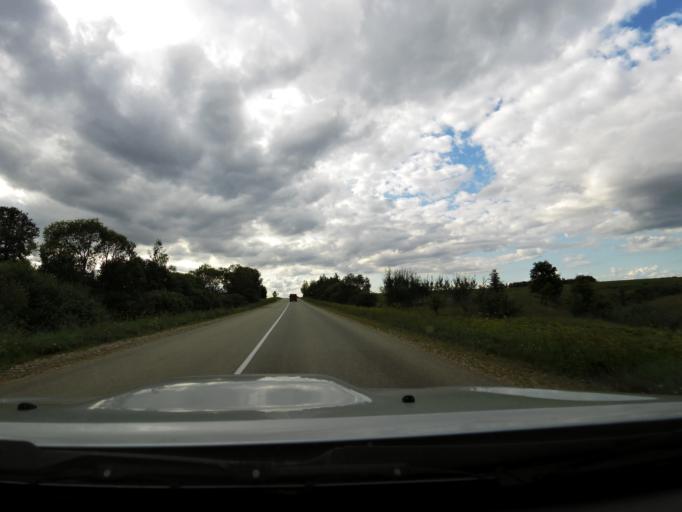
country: LV
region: Ilukste
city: Ilukste
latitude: 55.9789
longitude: 26.0086
